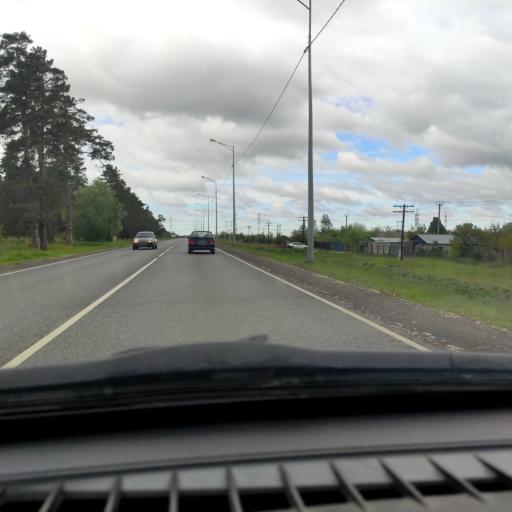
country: RU
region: Samara
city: Zhigulevsk
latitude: 53.5824
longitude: 49.5652
